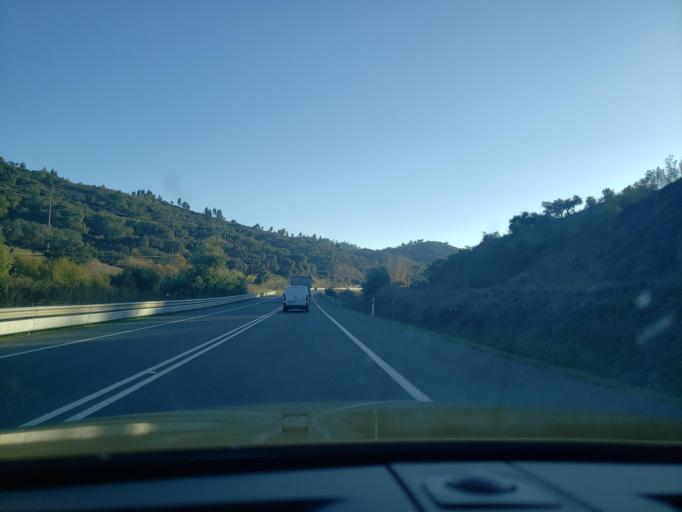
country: PT
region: Evora
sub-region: Portel
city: Portel
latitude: 38.3452
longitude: -7.6893
